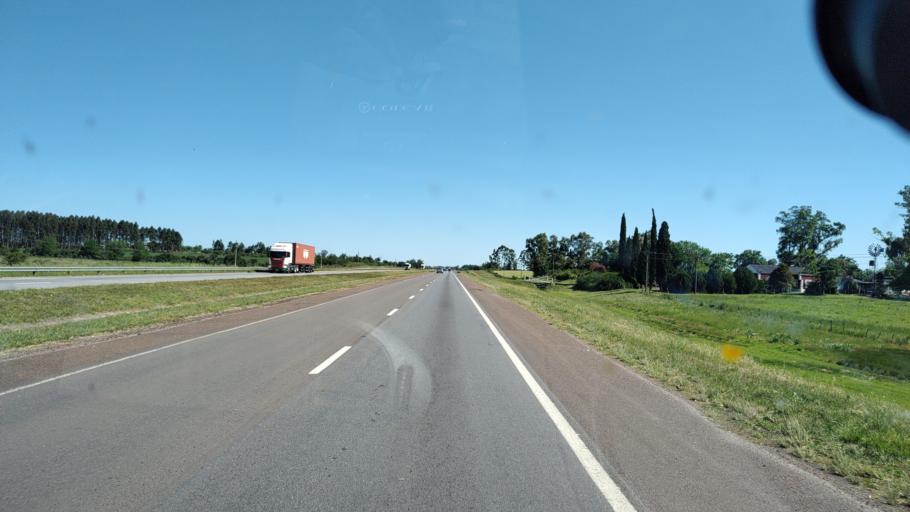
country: UY
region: Paysandu
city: San Felix
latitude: -32.3151
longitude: -58.2570
